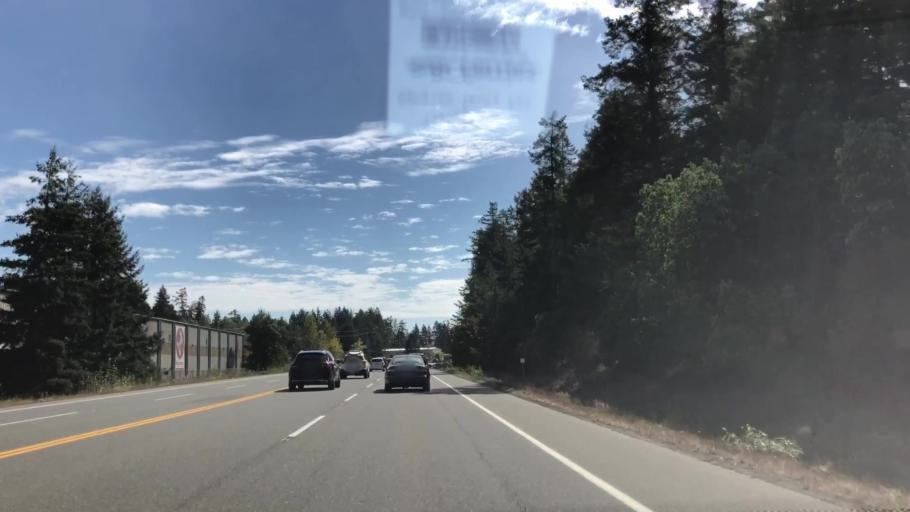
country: CA
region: British Columbia
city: Nanaimo
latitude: 49.1353
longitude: -123.8731
